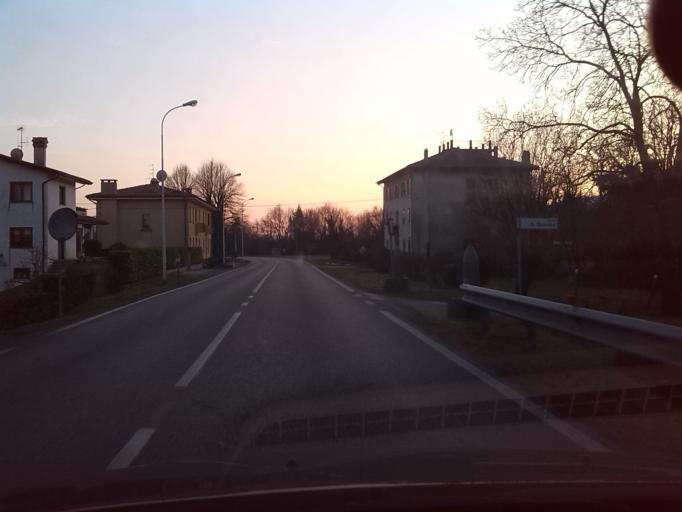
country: IT
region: Friuli Venezia Giulia
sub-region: Provincia di Udine
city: San Pietro al Natisone
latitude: 46.1239
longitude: 13.4833
